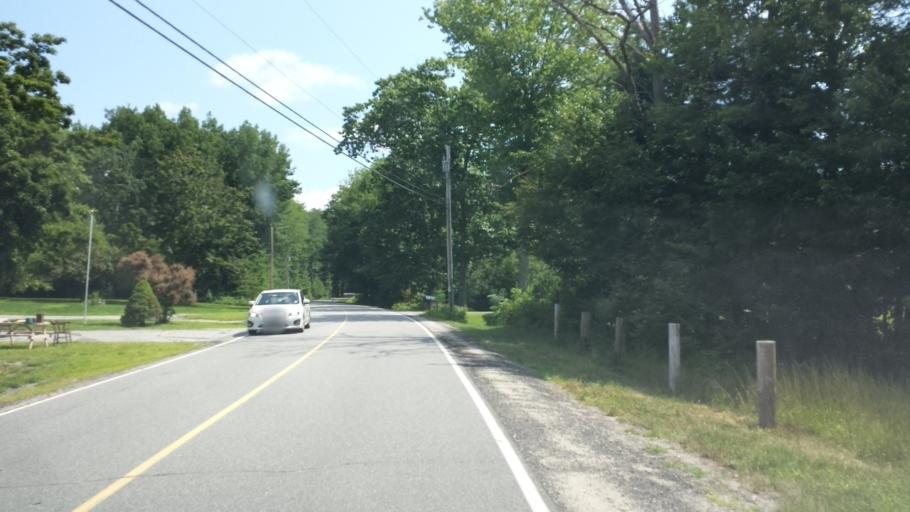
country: US
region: Maine
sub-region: York County
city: Kennebunk
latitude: 43.4460
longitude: -70.5224
